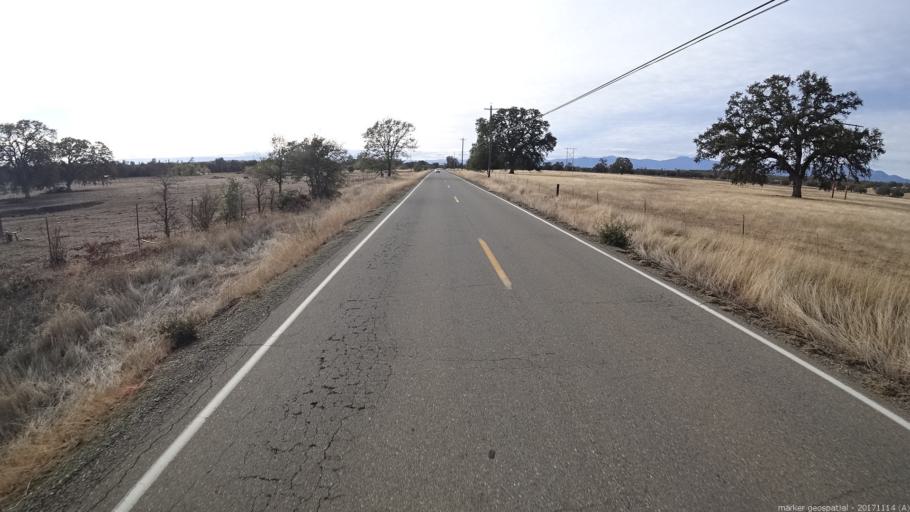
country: US
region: California
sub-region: Shasta County
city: Anderson
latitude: 40.3882
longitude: -122.4558
